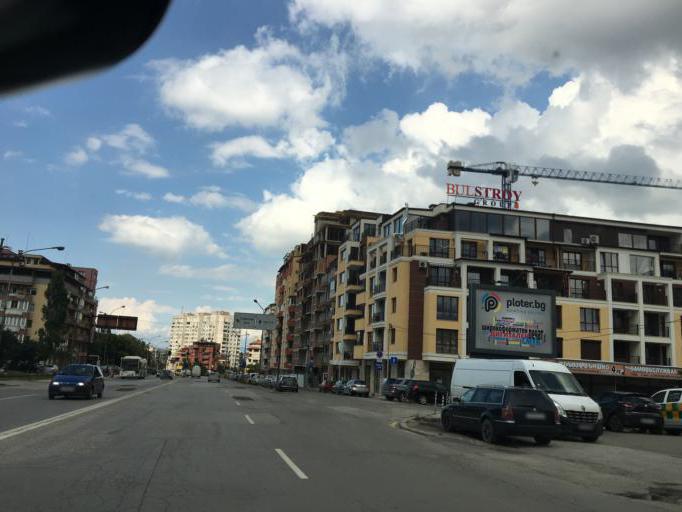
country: BG
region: Sofia-Capital
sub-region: Stolichna Obshtina
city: Sofia
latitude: 42.6498
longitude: 23.3575
